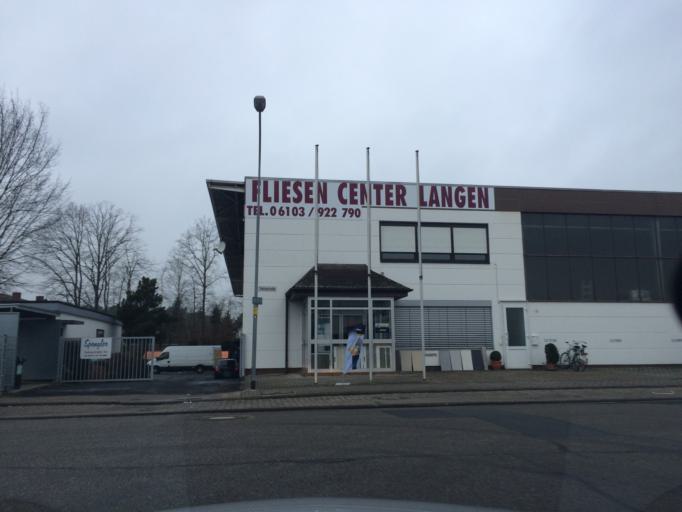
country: DE
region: Hesse
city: Langen
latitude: 50.0026
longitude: 8.6482
